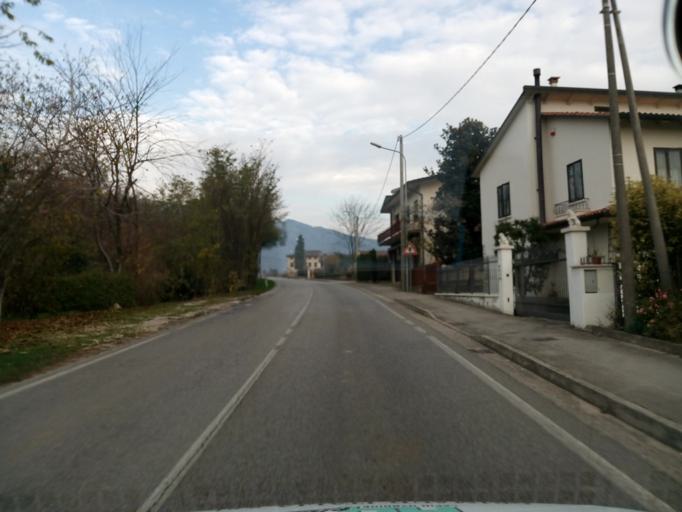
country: IT
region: Veneto
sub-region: Provincia di Treviso
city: Castelcucco
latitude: 45.8130
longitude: 11.8878
